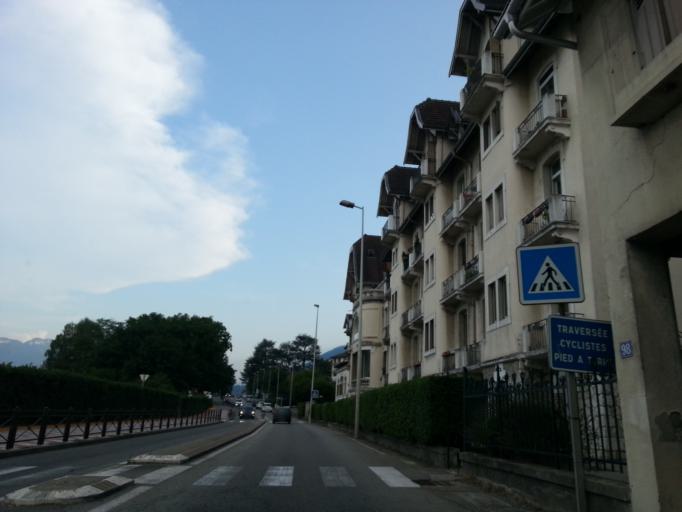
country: FR
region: Rhone-Alpes
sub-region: Departement de la Haute-Savoie
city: Sevrier
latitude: 45.8838
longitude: 6.1420
